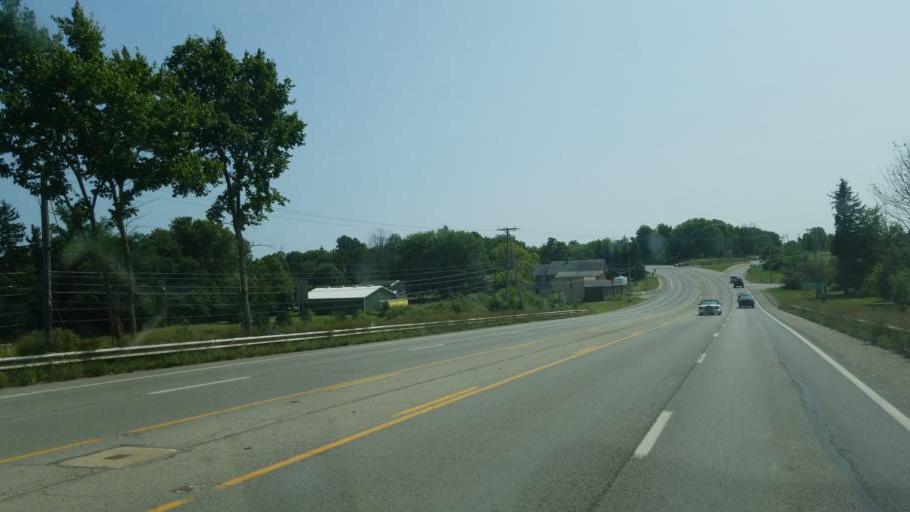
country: US
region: Ohio
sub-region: Richland County
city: Ontario
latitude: 40.8117
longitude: -82.5905
